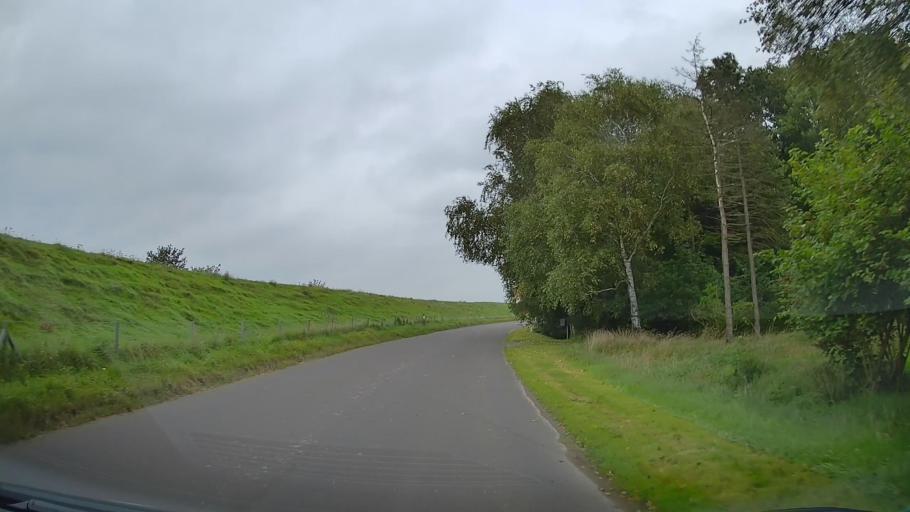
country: DE
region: Lower Saxony
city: Geversdorf
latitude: 53.8246
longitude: 9.0716
